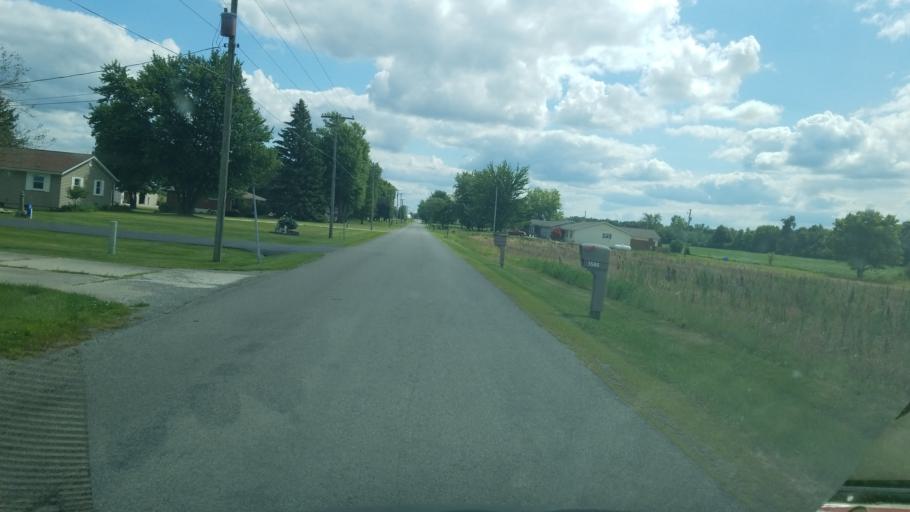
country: US
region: Ohio
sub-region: Allen County
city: Lima
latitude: 40.7613
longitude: -83.9942
